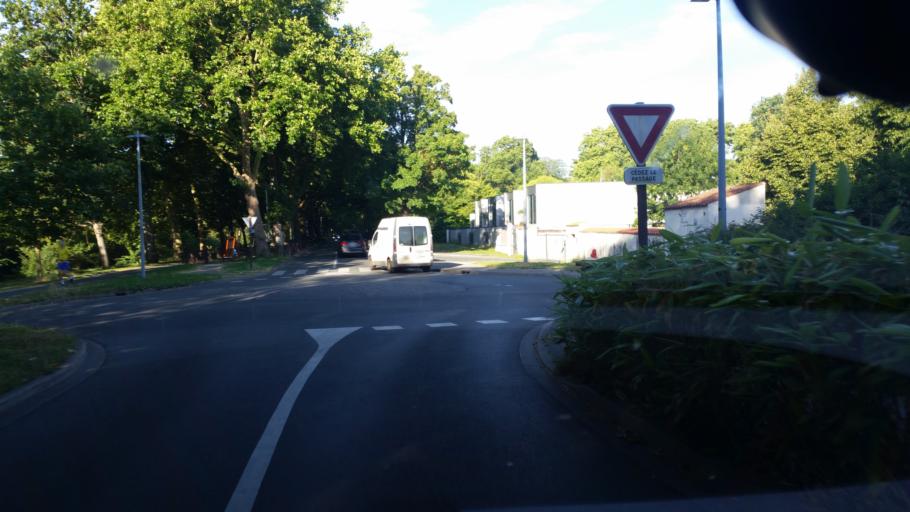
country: FR
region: Poitou-Charentes
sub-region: Departement de la Charente-Maritime
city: Perigny
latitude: 46.1662
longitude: -1.1111
